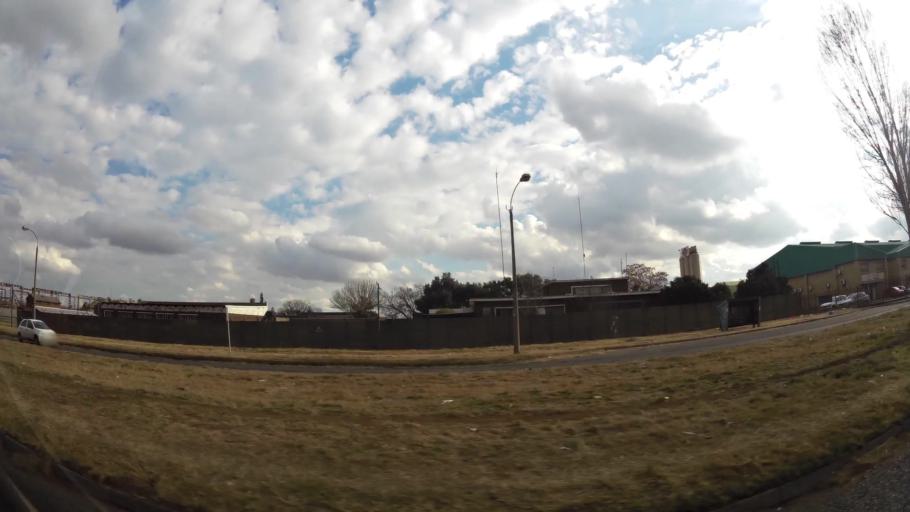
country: ZA
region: Orange Free State
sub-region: Fezile Dabi District Municipality
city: Sasolburg
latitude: -26.8237
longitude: 27.8362
